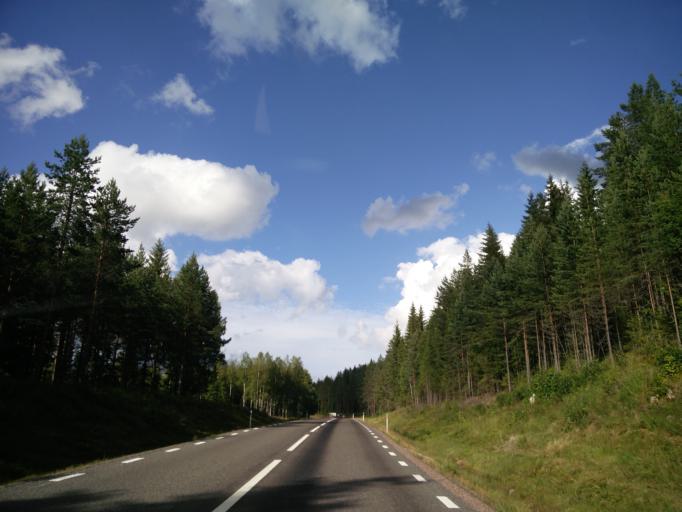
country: SE
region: Vaermland
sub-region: Torsby Kommun
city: Torsby
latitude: 60.3369
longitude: 13.1460
